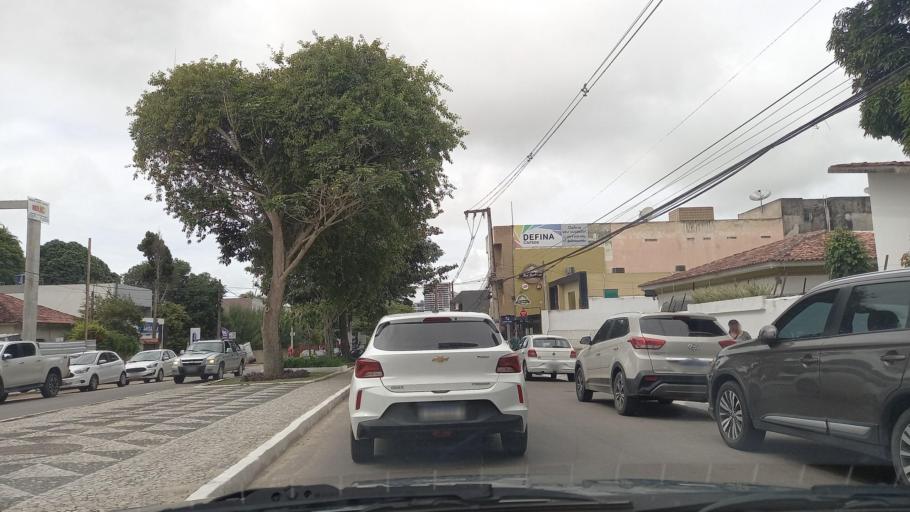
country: BR
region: Pernambuco
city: Garanhuns
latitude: -8.8856
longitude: -36.4843
